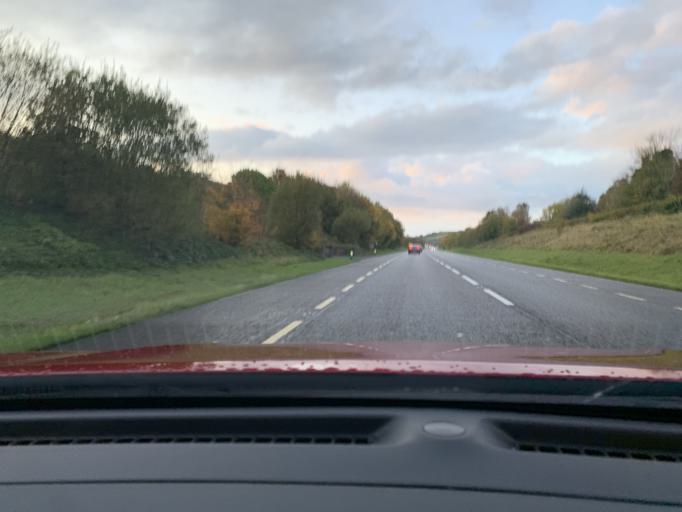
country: IE
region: Connaught
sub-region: Roscommon
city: Boyle
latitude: 54.0673
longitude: -8.3610
